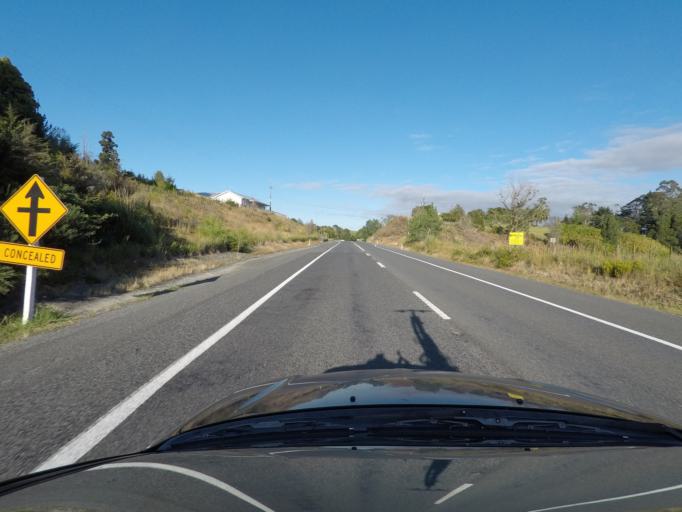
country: NZ
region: Northland
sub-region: Far North District
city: Kawakawa
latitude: -35.5204
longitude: 174.2021
